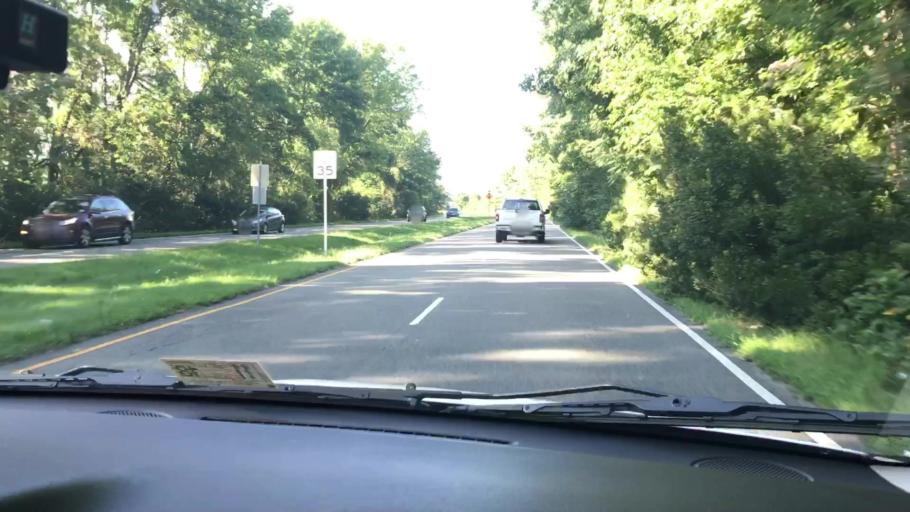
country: US
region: Virginia
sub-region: City of Hampton
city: Hampton
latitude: 37.0603
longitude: -76.3658
